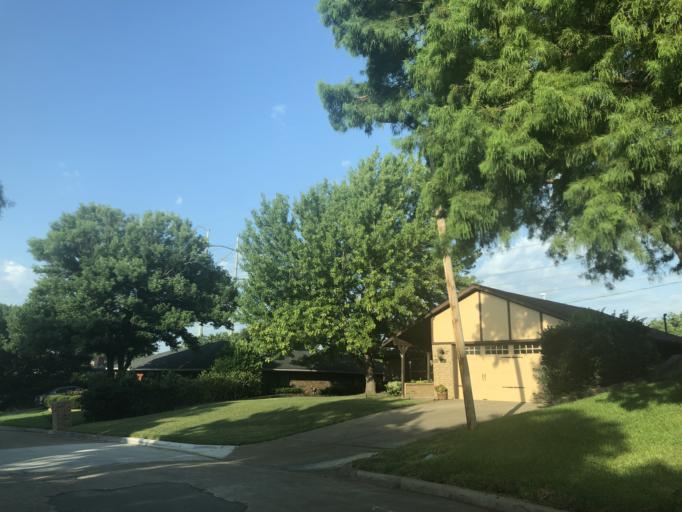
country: US
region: Texas
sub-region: Dallas County
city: Grand Prairie
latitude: 32.7716
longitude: -97.0310
